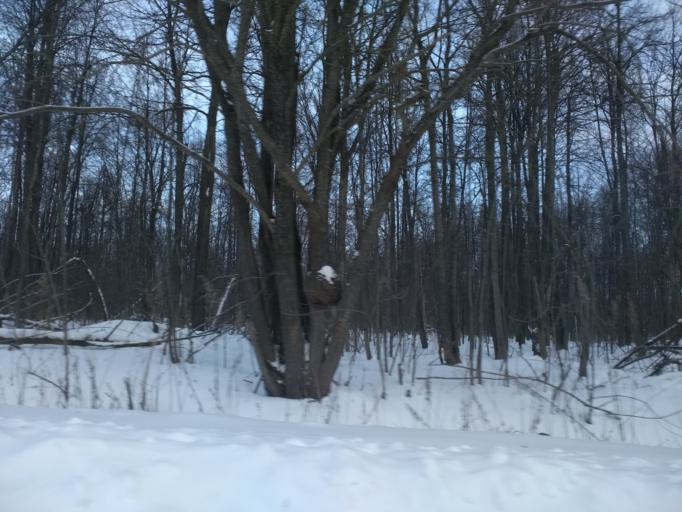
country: RU
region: Bashkortostan
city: Kudeyevskiy
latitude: 54.7119
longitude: 56.6468
